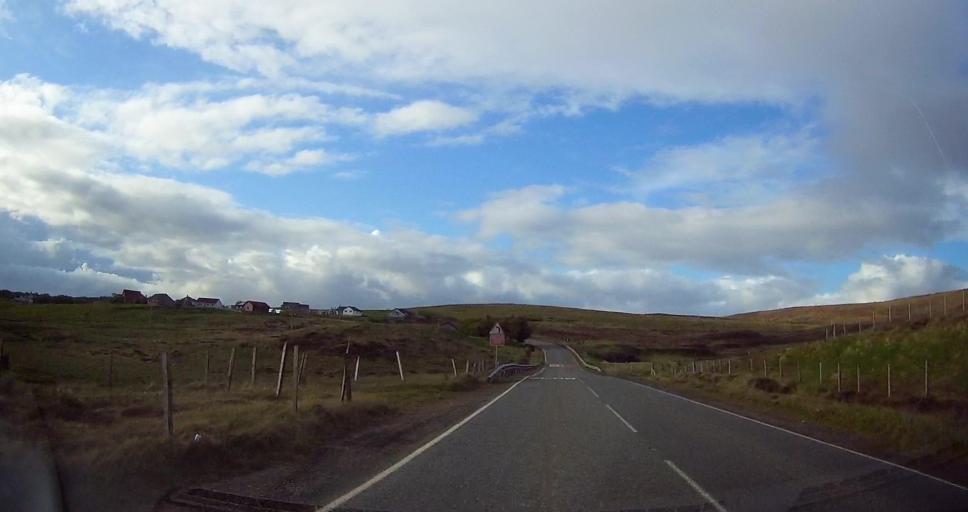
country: GB
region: Scotland
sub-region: Shetland Islands
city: Lerwick
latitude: 60.3831
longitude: -1.3426
